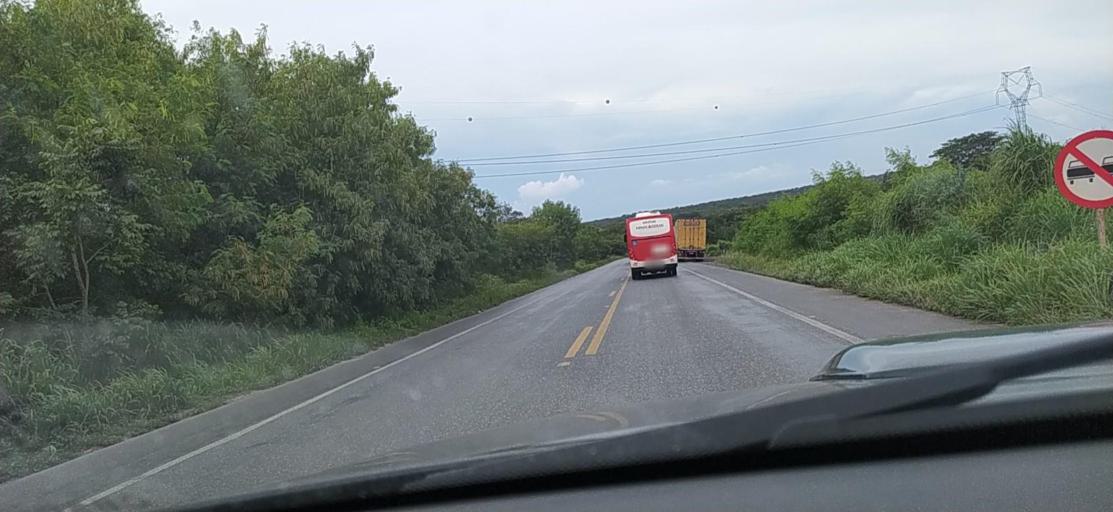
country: BR
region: Minas Gerais
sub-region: Montes Claros
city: Montes Claros
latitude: -16.6664
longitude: -43.7864
